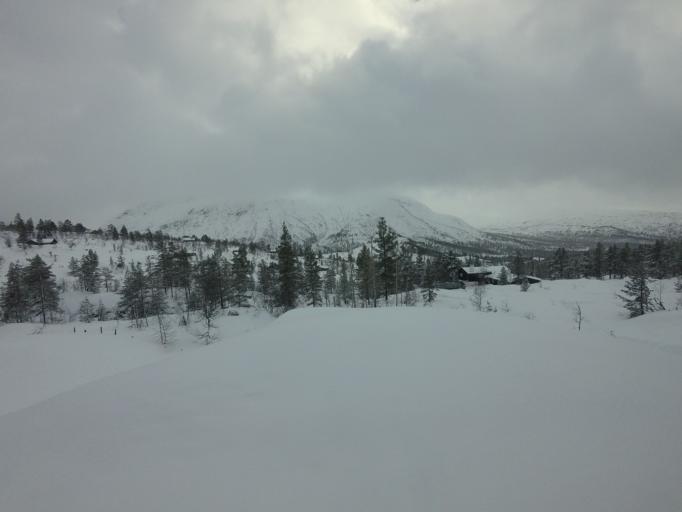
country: NO
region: Hordaland
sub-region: Ulvik
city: Ulvik
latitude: 60.7090
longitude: 6.8966
